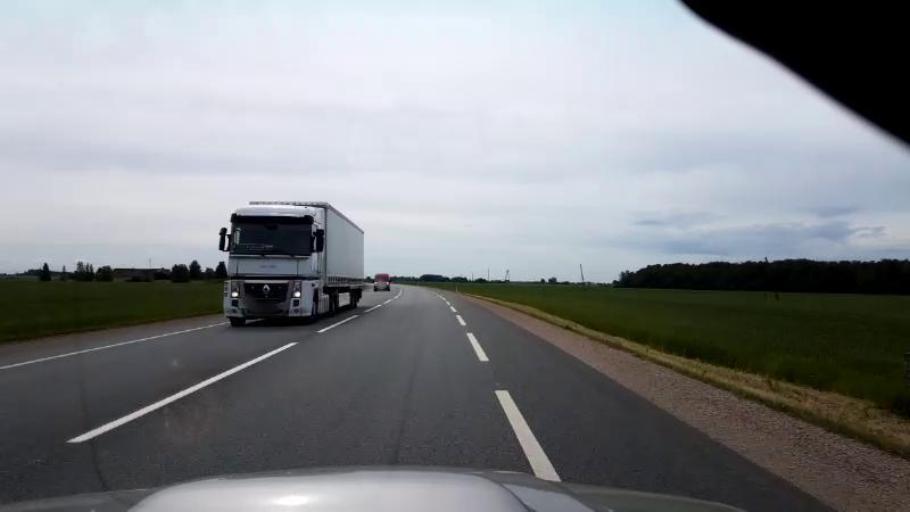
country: LV
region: Bauskas Rajons
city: Bauska
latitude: 56.4451
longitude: 24.1658
